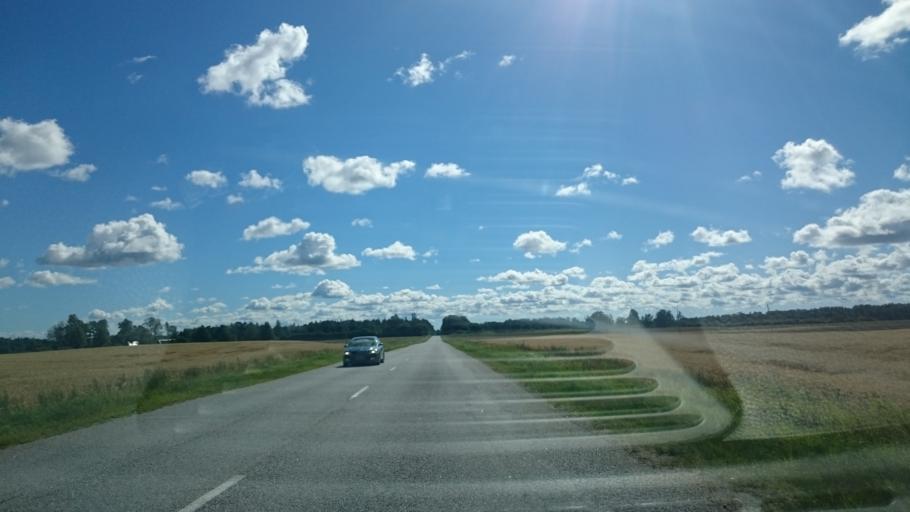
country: LV
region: Aizpute
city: Aizpute
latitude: 56.8214
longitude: 21.7327
